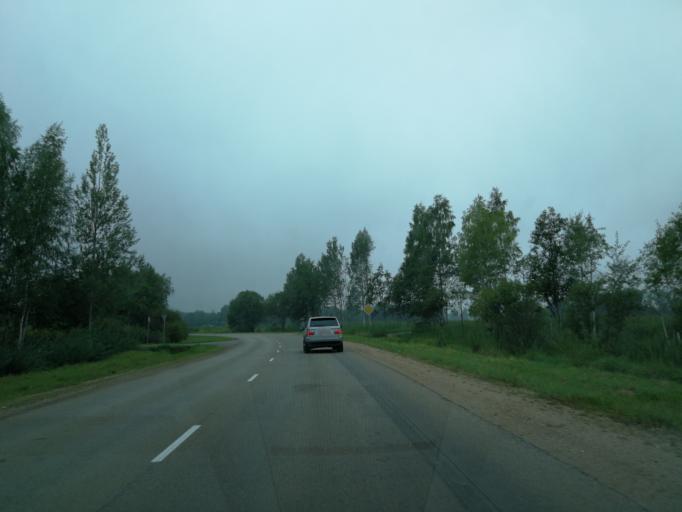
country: LV
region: Preilu Rajons
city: Preili
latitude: 56.3023
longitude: 26.7208
